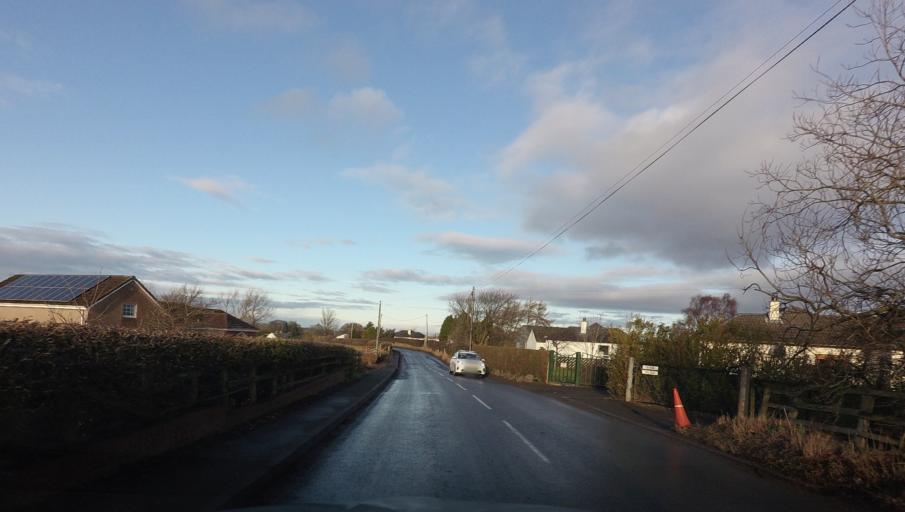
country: GB
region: Scotland
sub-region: West Lothian
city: East Calder
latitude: 55.8964
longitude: -3.4433
